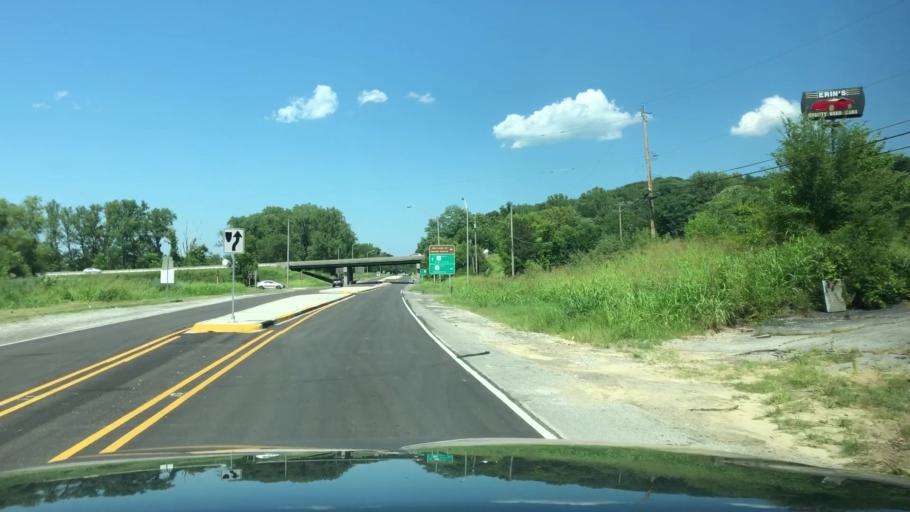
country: US
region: Illinois
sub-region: Saint Clair County
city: Alorton
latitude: 38.5661
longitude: -90.0930
